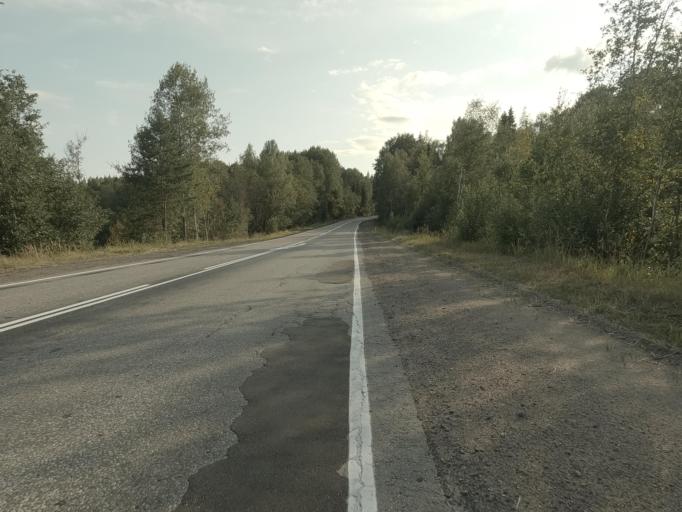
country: RU
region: Leningrad
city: Vyborg
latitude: 60.8445
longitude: 28.8538
